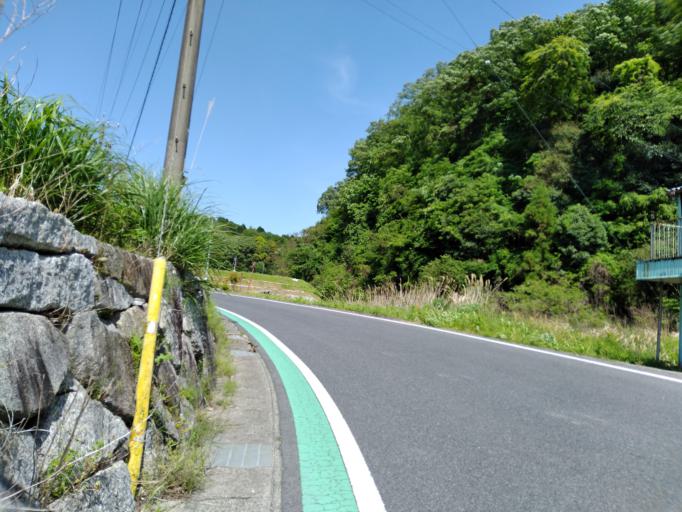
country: JP
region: Gifu
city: Toki
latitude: 35.2453
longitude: 137.2310
